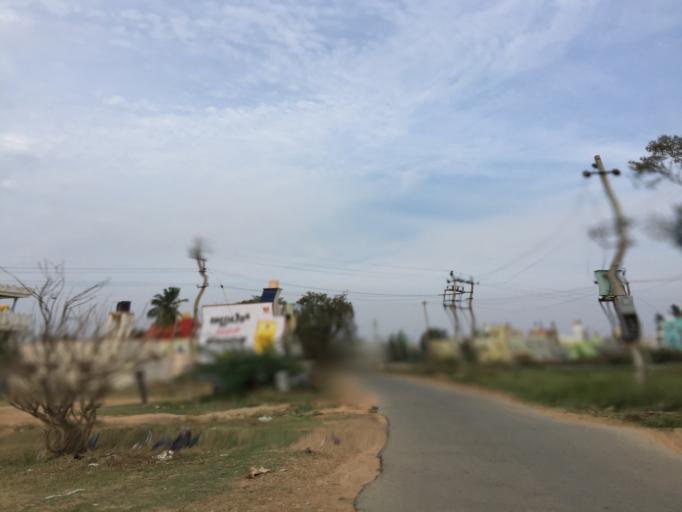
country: IN
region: Karnataka
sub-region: Kolar
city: Kolar
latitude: 13.1373
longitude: 78.1137
